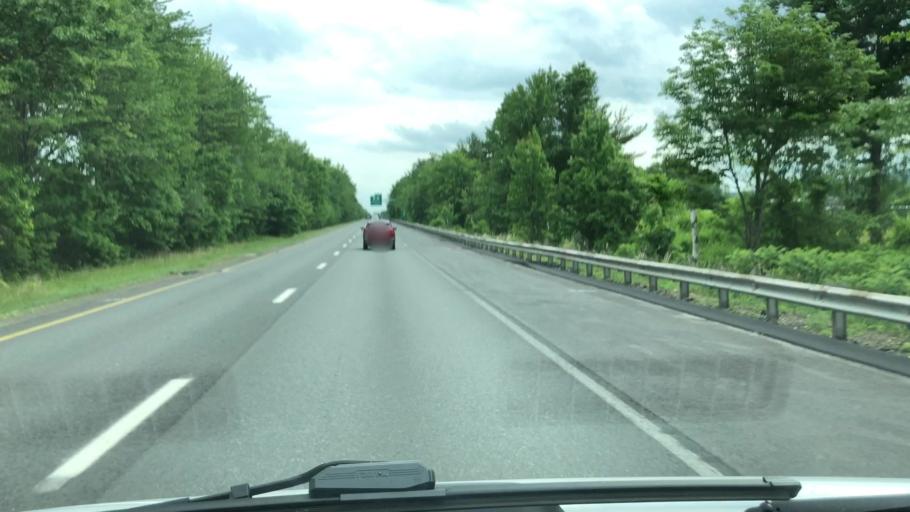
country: US
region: Massachusetts
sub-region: Franklin County
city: Whately
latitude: 42.4442
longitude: -72.6201
